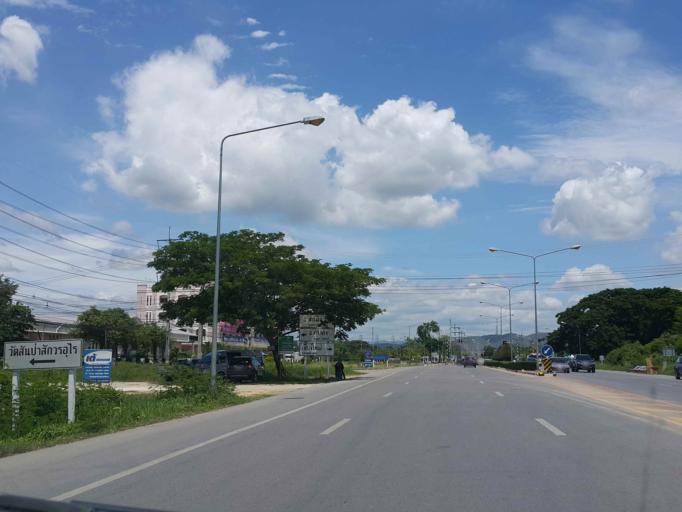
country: TH
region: Chiang Mai
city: Hang Dong
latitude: 18.7225
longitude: 98.9481
